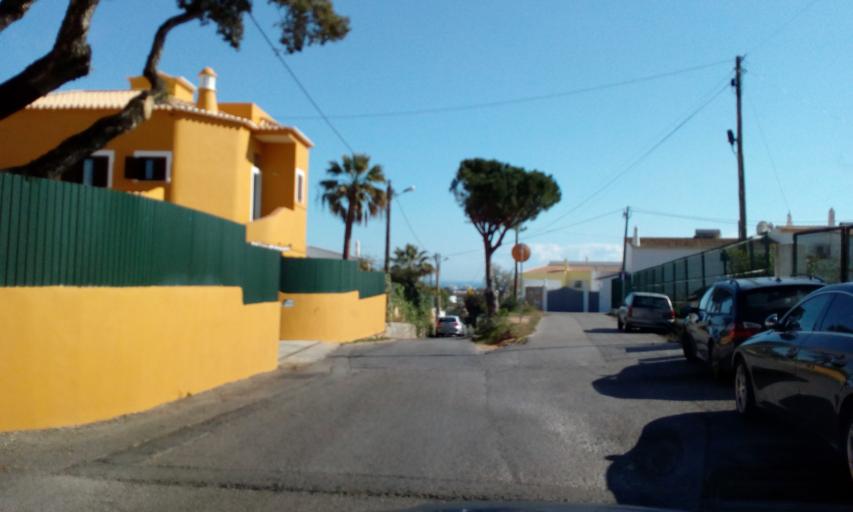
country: PT
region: Faro
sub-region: Albufeira
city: Ferreiras
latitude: 37.1069
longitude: -8.2113
